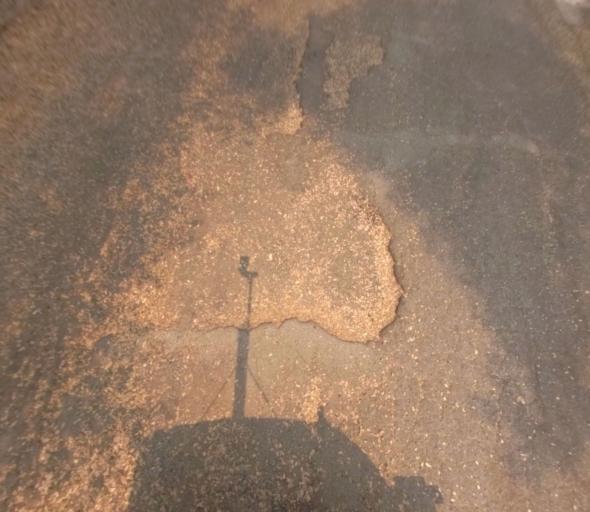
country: US
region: California
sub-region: Madera County
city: Oakhurst
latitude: 37.3193
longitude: -119.6063
